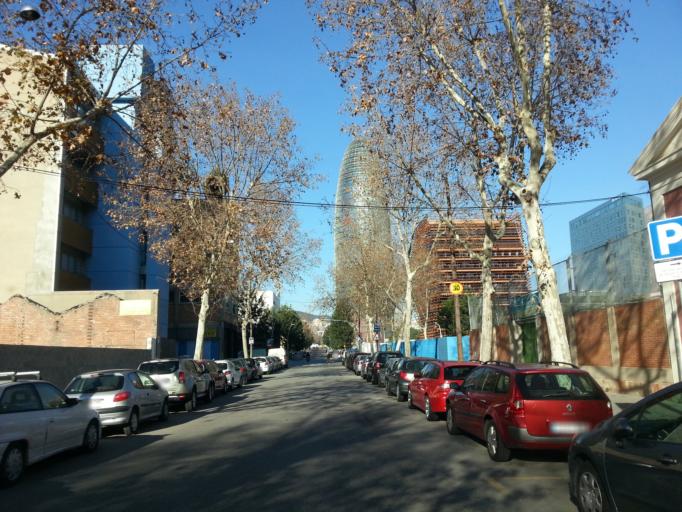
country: ES
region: Catalonia
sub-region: Provincia de Barcelona
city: Sant Marti
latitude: 41.4009
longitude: 2.1924
